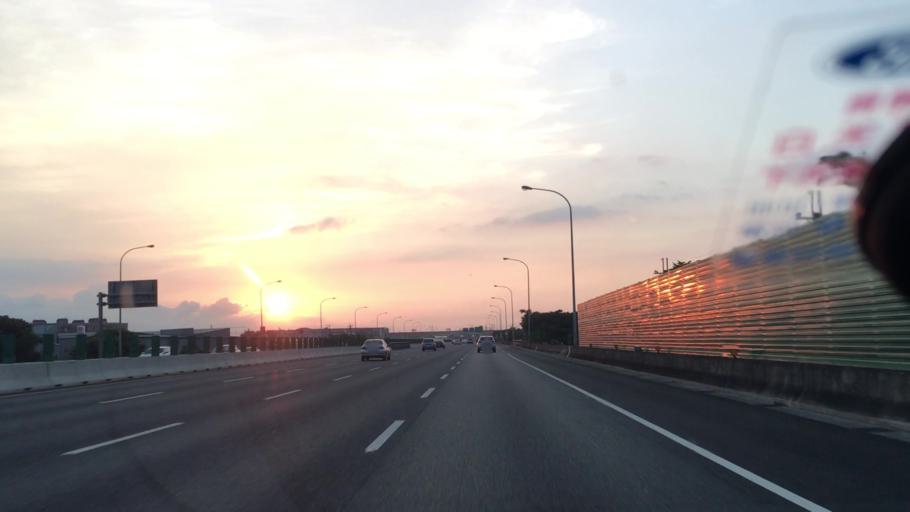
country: TW
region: Taiwan
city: Taoyuan City
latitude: 25.0297
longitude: 121.2490
